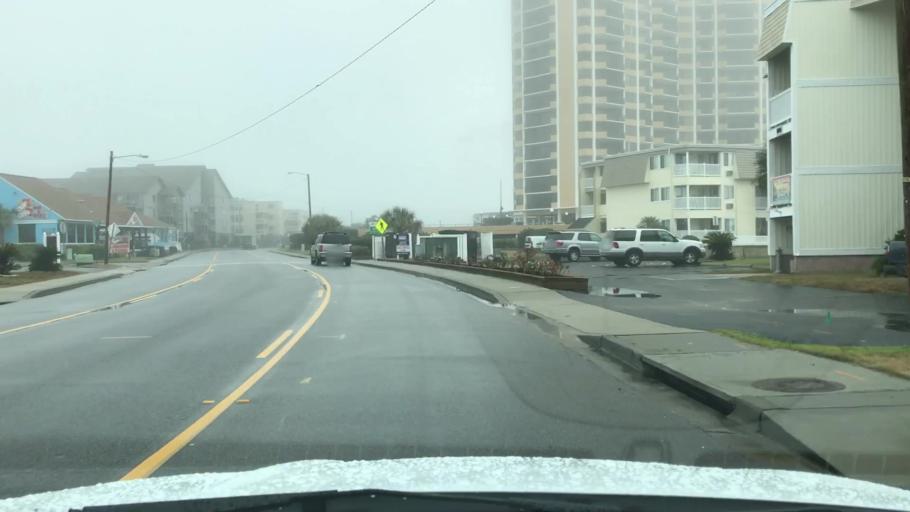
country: US
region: South Carolina
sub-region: Horry County
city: North Myrtle Beach
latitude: 33.7614
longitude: -78.7878
